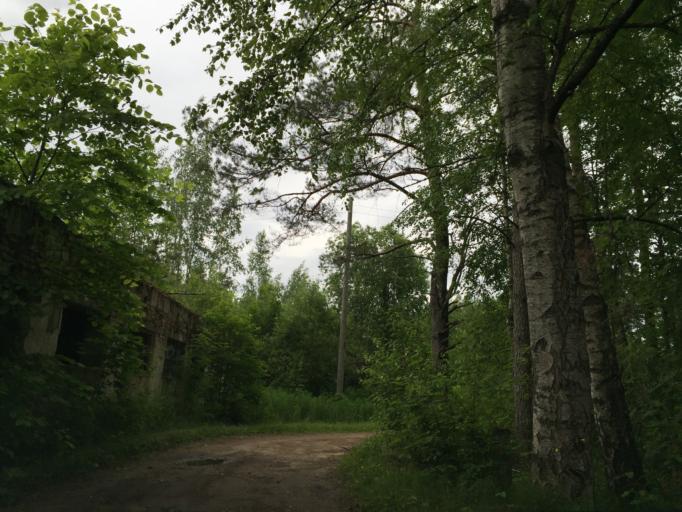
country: LV
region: Apes Novads
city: Ape
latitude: 57.4209
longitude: 26.3686
